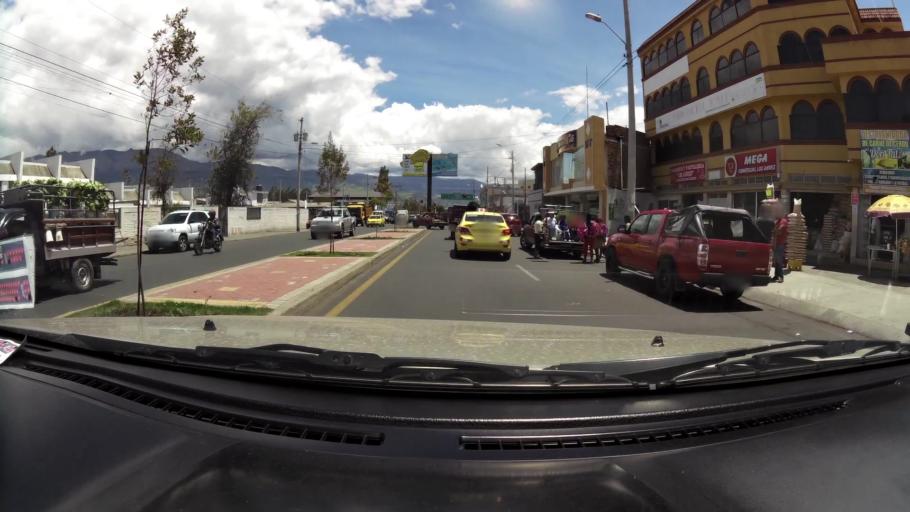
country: EC
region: Chimborazo
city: Riobamba
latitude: -1.6885
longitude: -78.6326
